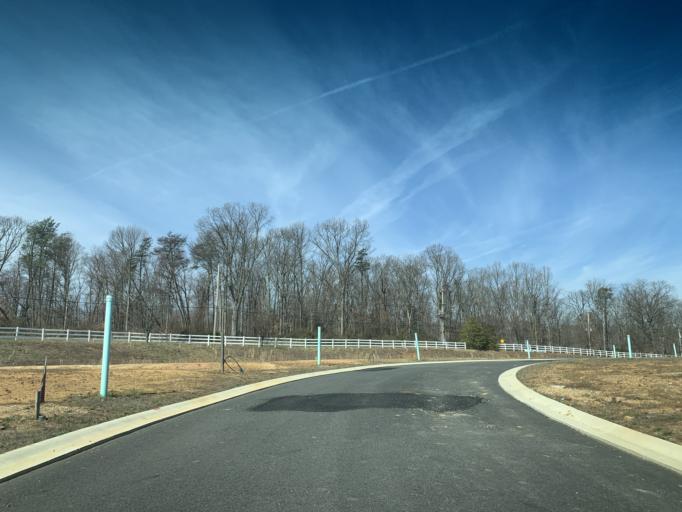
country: US
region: Maryland
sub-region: Cecil County
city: Charlestown
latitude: 39.5552
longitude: -76.0104
